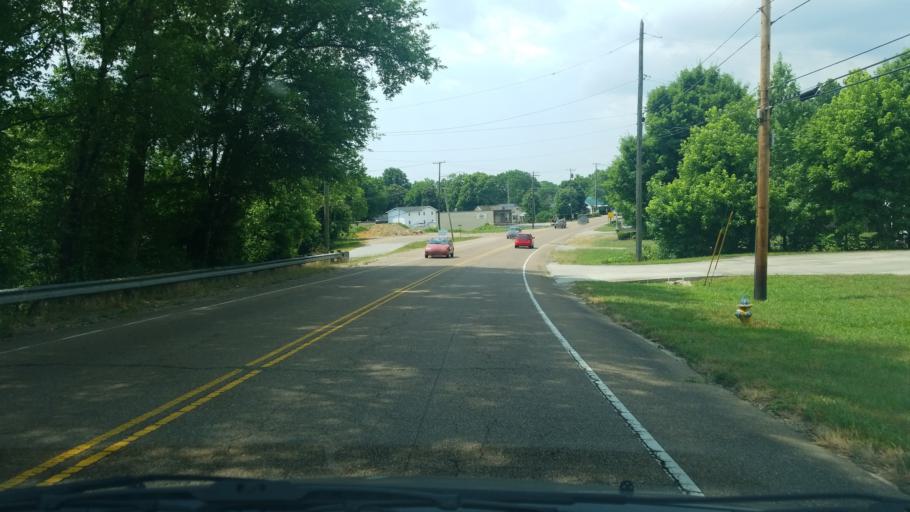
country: US
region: Tennessee
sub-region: Hamilton County
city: Soddy-Daisy
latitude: 35.2492
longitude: -85.1853
